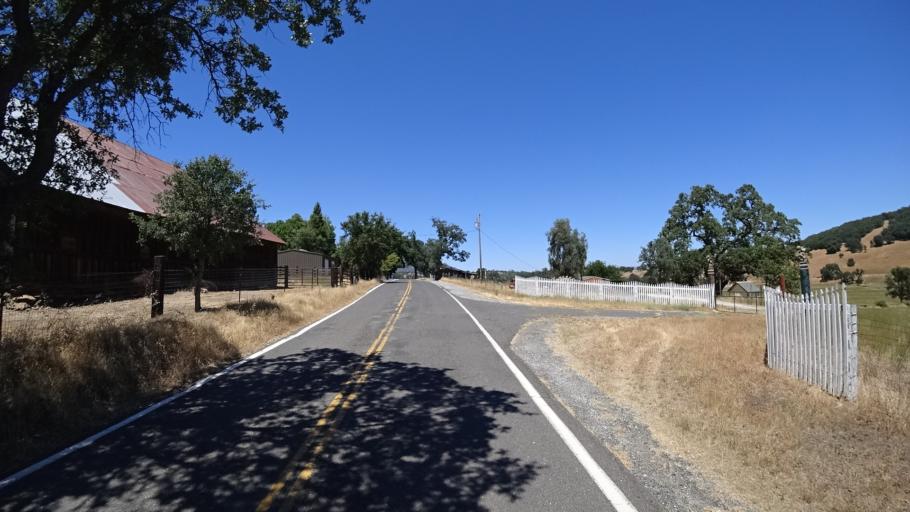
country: US
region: California
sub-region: Calaveras County
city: Copperopolis
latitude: 38.0771
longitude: -120.6655
